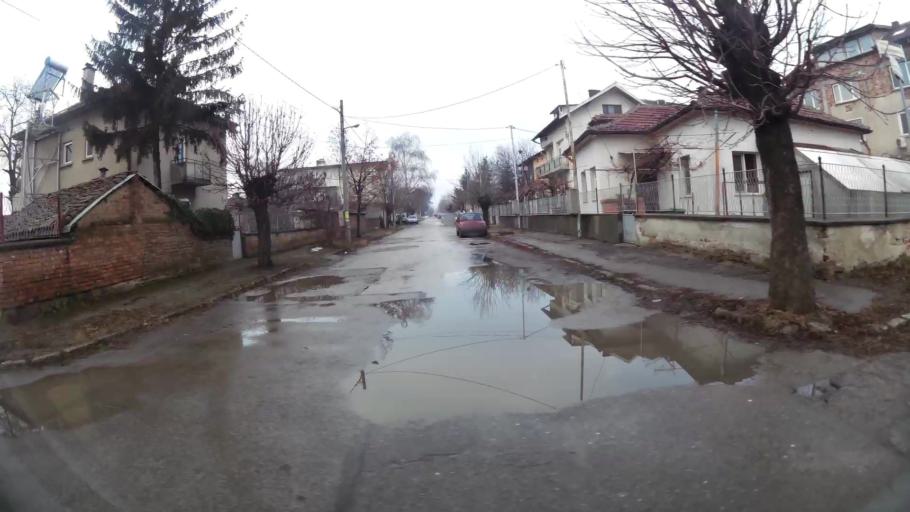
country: BG
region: Sofia-Capital
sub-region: Stolichna Obshtina
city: Sofia
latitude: 42.7359
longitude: 23.3452
